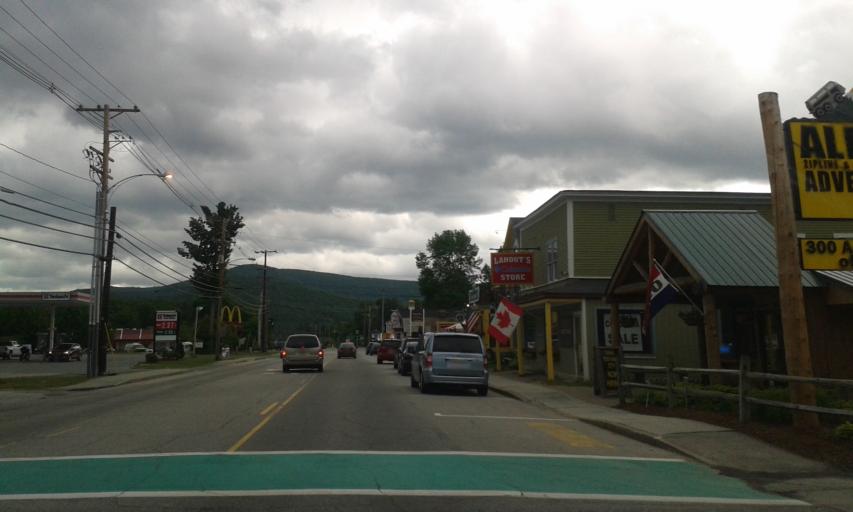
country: US
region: New Hampshire
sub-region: Grafton County
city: Woodstock
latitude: 44.0391
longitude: -71.6745
